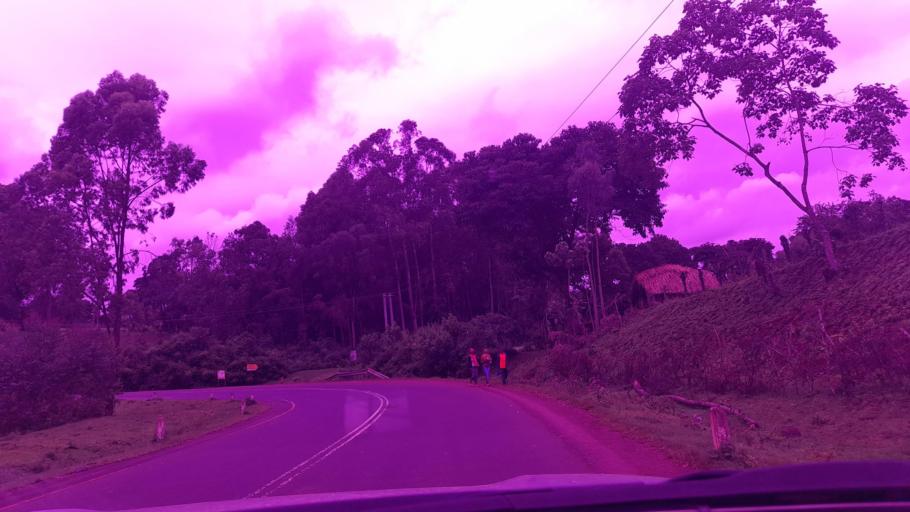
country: ET
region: Southern Nations, Nationalities, and People's Region
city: Bonga
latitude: 7.2919
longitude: 35.9770
